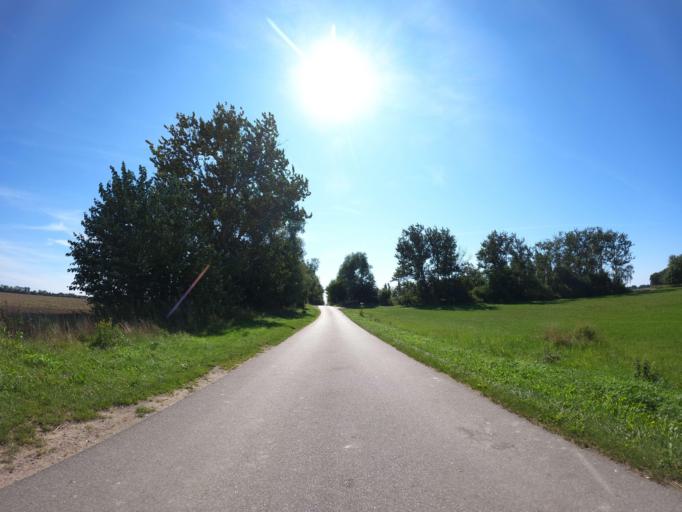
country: DE
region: Mecklenburg-Vorpommern
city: Prohn
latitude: 54.3869
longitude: 13.0279
